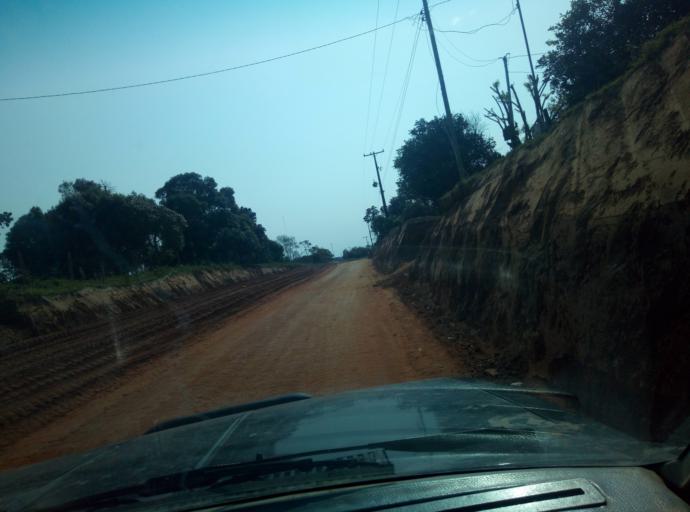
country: PY
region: Caaguazu
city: Carayao
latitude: -25.3276
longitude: -56.3308
